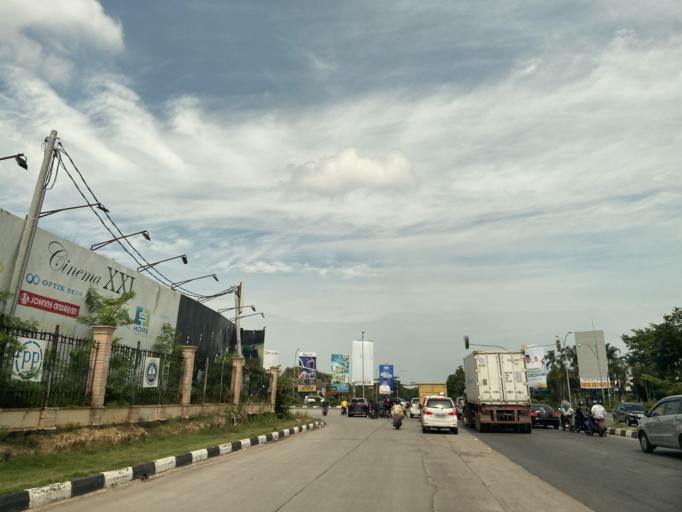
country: SG
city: Singapore
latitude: 1.1183
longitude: 104.0454
